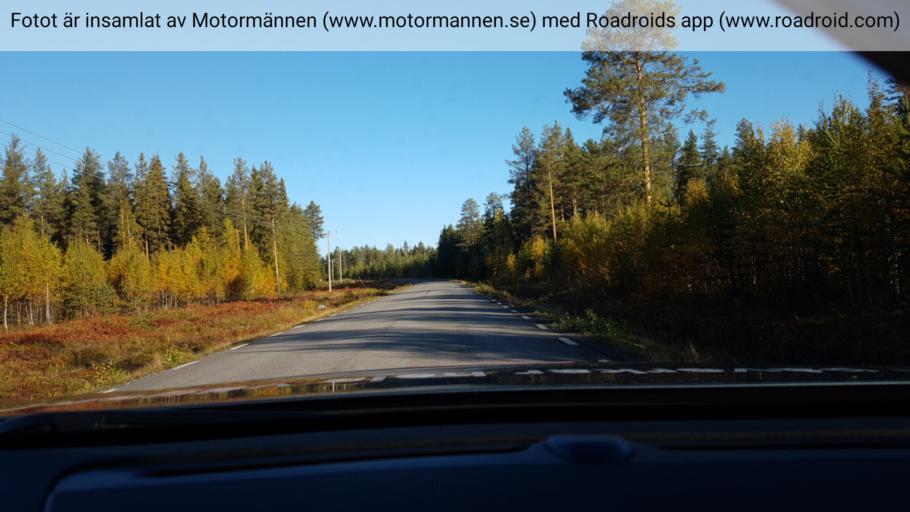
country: SE
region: Norrbotten
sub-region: Bodens Kommun
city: Boden
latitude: 65.9278
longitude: 21.6528
